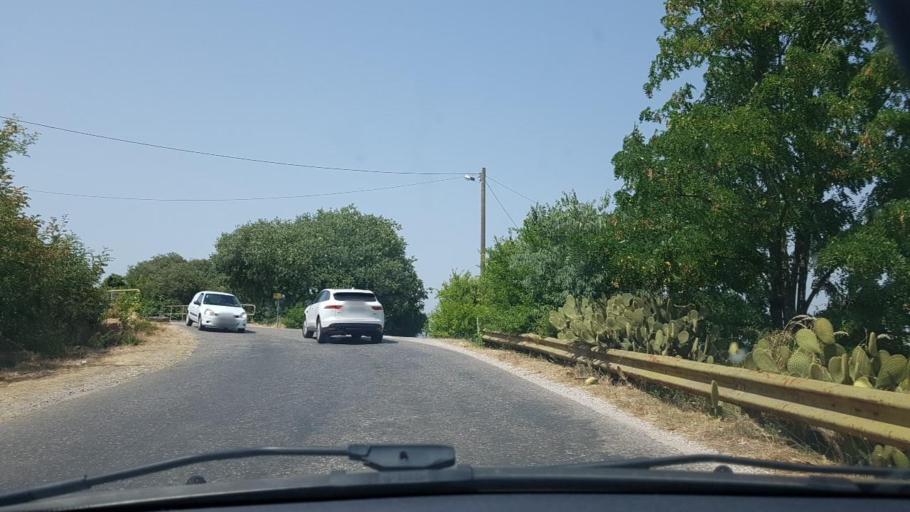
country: HR
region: Dubrovacko-Neretvanska
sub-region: Grad Dubrovnik
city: Metkovic
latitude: 43.0494
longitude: 17.7014
